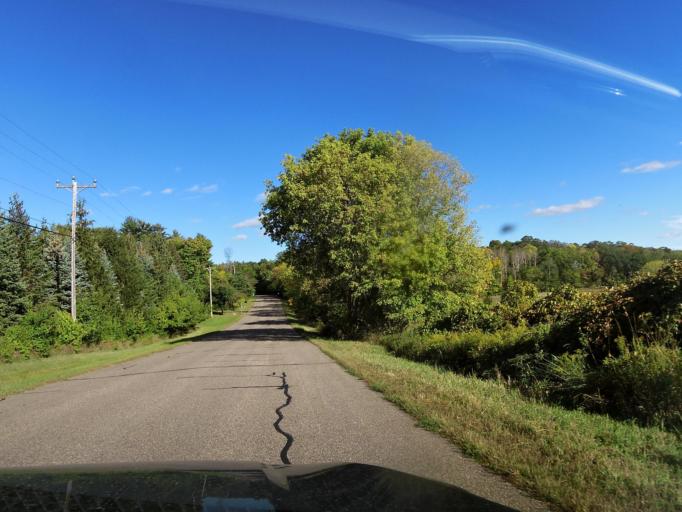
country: US
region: Minnesota
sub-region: Washington County
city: Afton
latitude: 44.8764
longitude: -92.8088
